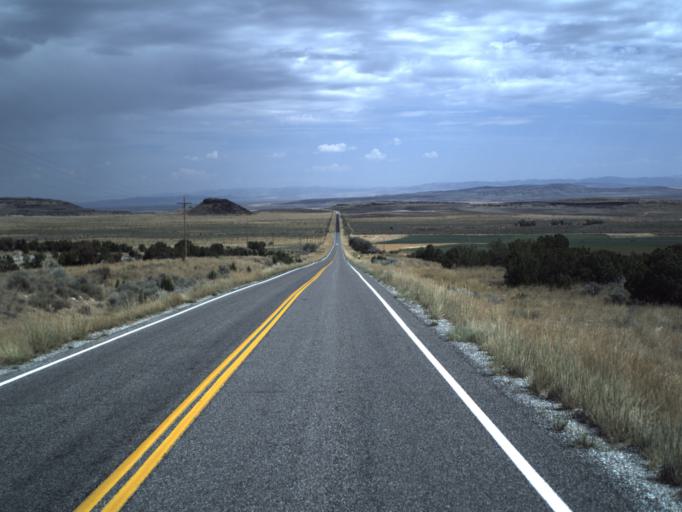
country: US
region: Idaho
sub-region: Cassia County
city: Burley
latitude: 41.8168
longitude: -113.2070
